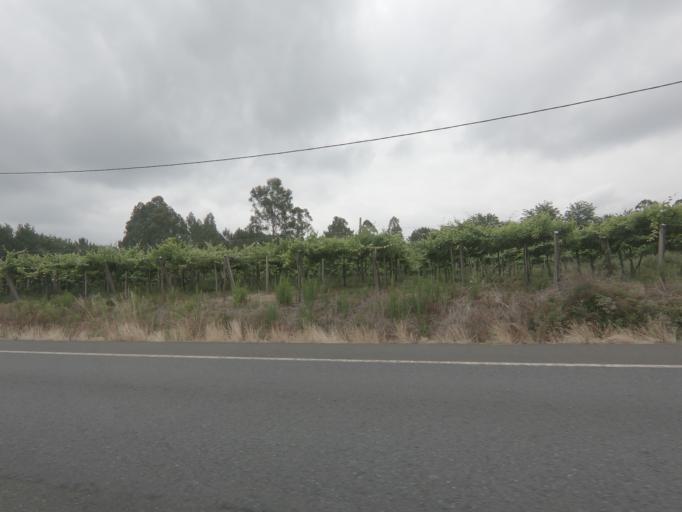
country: ES
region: Galicia
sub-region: Provincia de Pontevedra
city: Tomino
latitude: 41.9699
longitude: -8.7574
